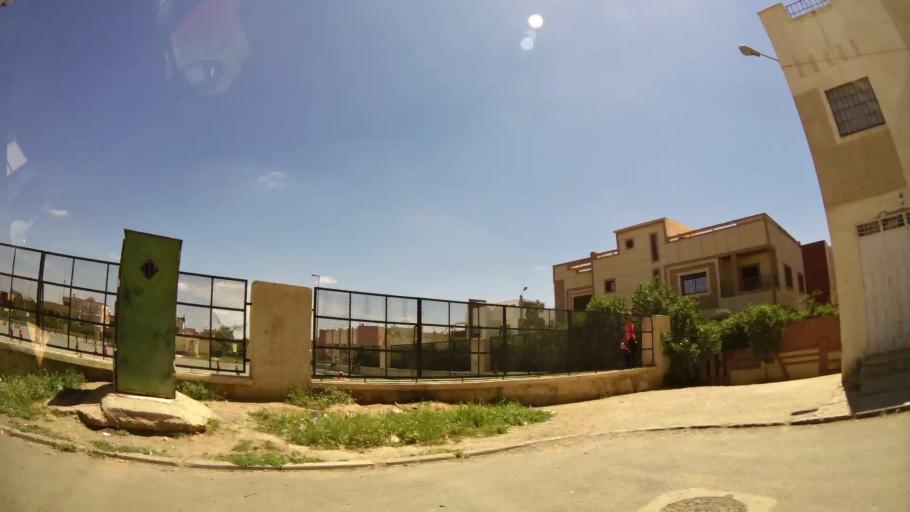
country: MA
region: Oriental
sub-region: Oujda-Angad
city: Oujda
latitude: 34.6613
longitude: -1.9466
